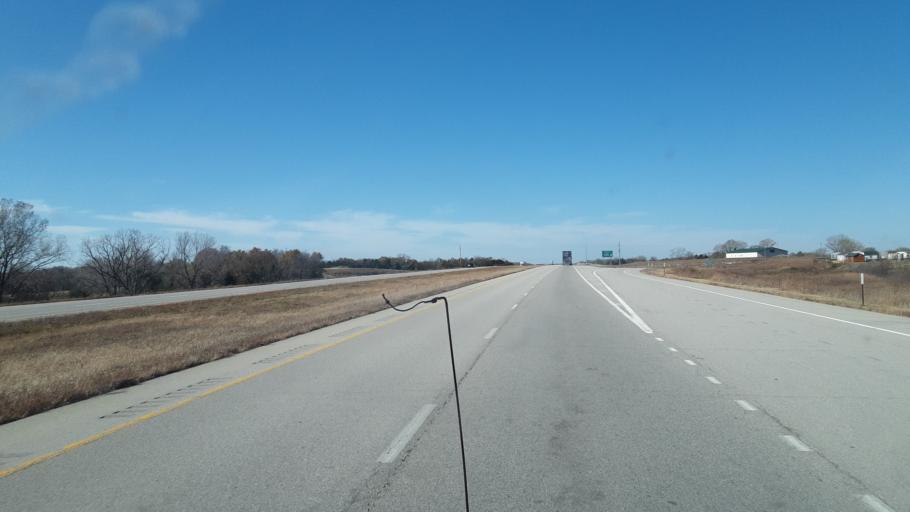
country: US
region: Kansas
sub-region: Lyon County
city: Emporia
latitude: 38.4104
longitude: -96.0910
